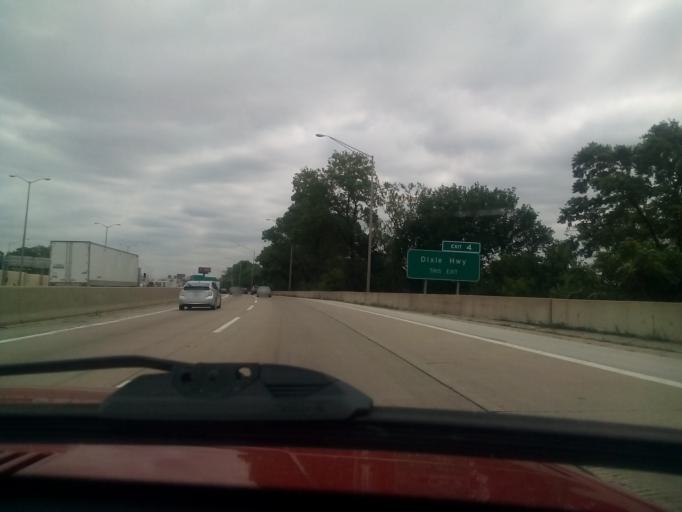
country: US
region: Illinois
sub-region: Cook County
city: University Park
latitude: 41.5781
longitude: -87.6733
